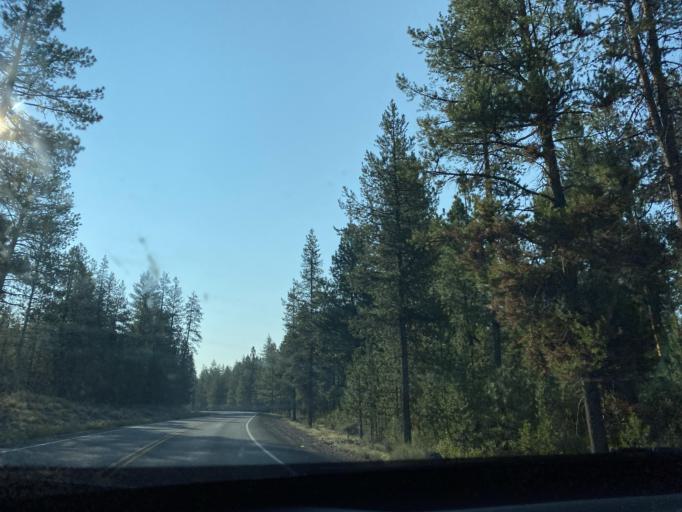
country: US
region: Oregon
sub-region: Deschutes County
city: La Pine
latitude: 43.7075
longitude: -121.4022
